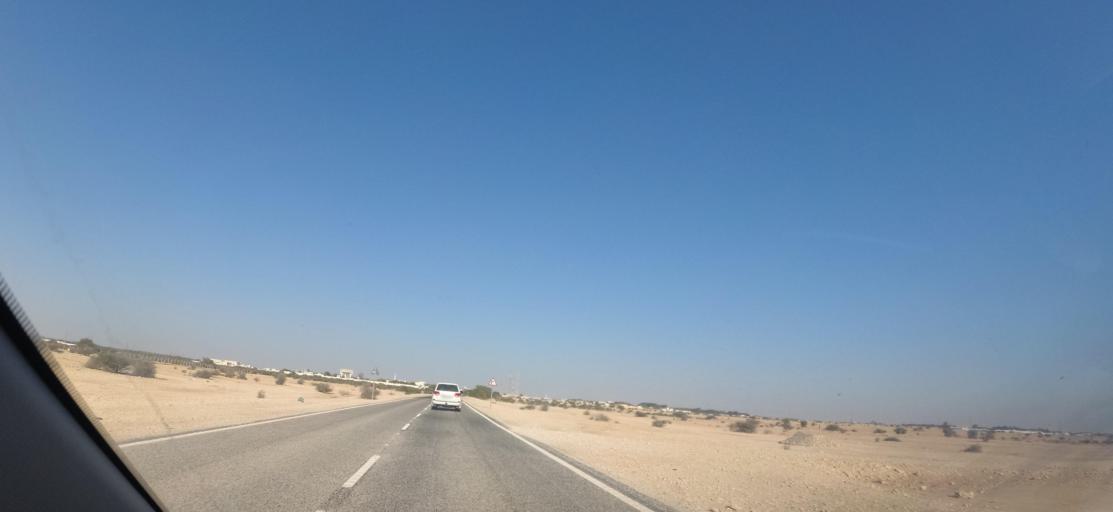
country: QA
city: Al Ghuwayriyah
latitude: 25.8206
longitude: 51.2378
